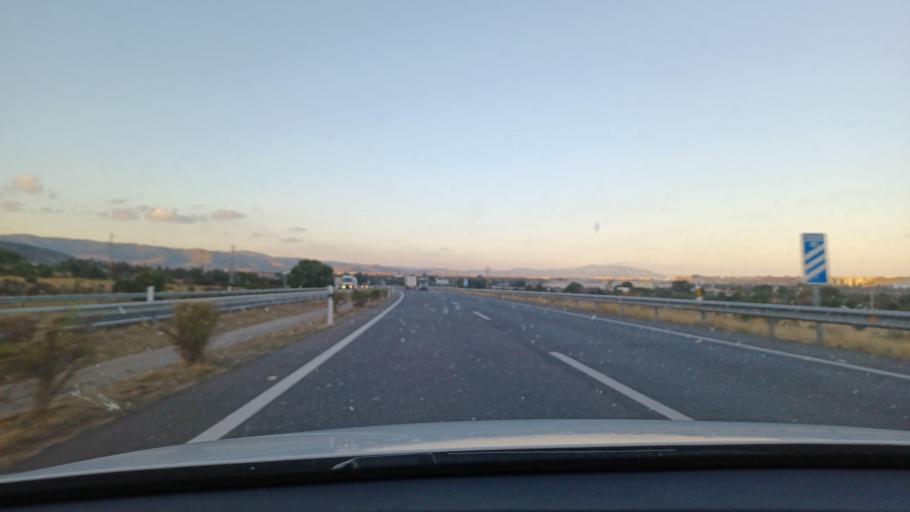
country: ES
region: Valencia
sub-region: Provincia de Castello
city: Orpesa/Oropesa del Mar
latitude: 40.1006
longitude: 0.1296
